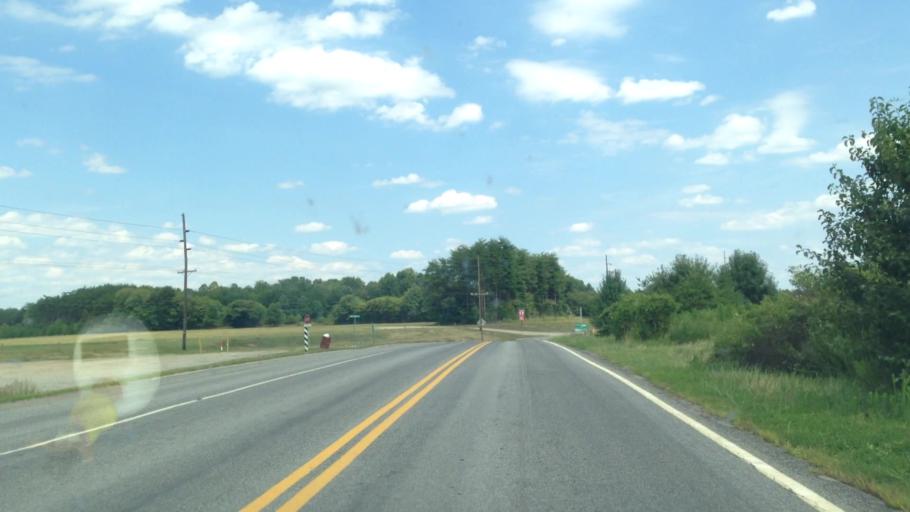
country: US
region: Virginia
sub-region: Henry County
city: Chatmoss
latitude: 36.6276
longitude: -79.8580
